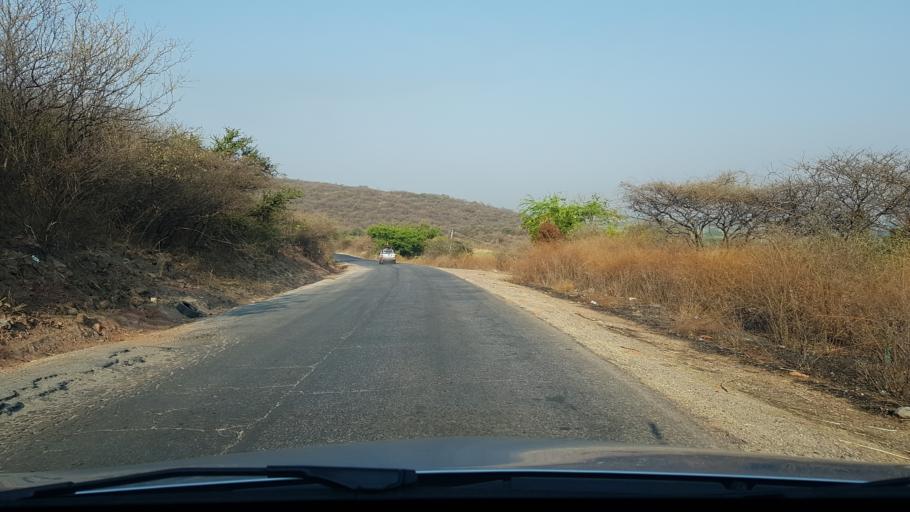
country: MX
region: Morelos
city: Tlaltizapan
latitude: 18.6788
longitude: -99.0828
